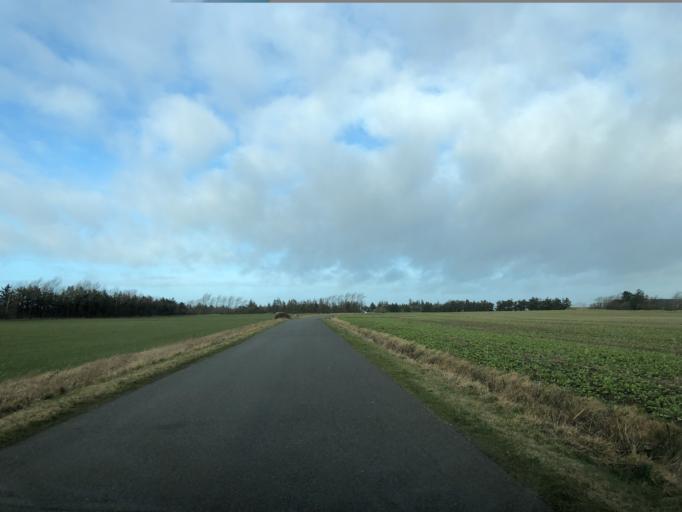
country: DK
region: Central Jutland
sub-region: Holstebro Kommune
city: Ulfborg
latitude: 56.3081
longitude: 8.2120
